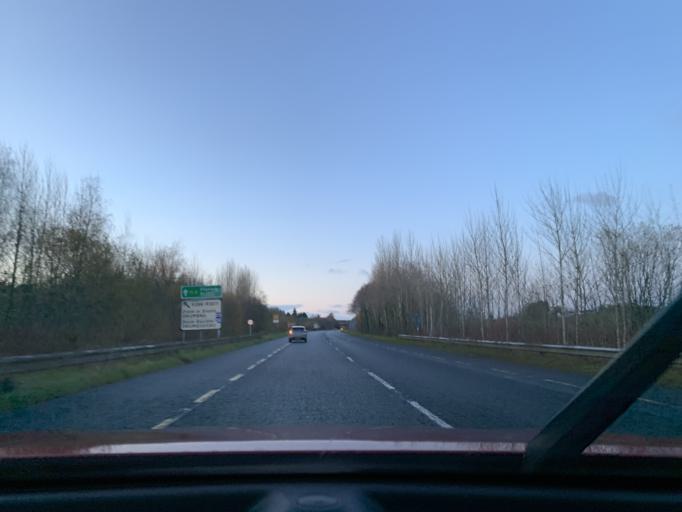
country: IE
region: Connaught
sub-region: County Leitrim
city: Carrick-on-Shannon
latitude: 53.9256
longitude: -7.9966
